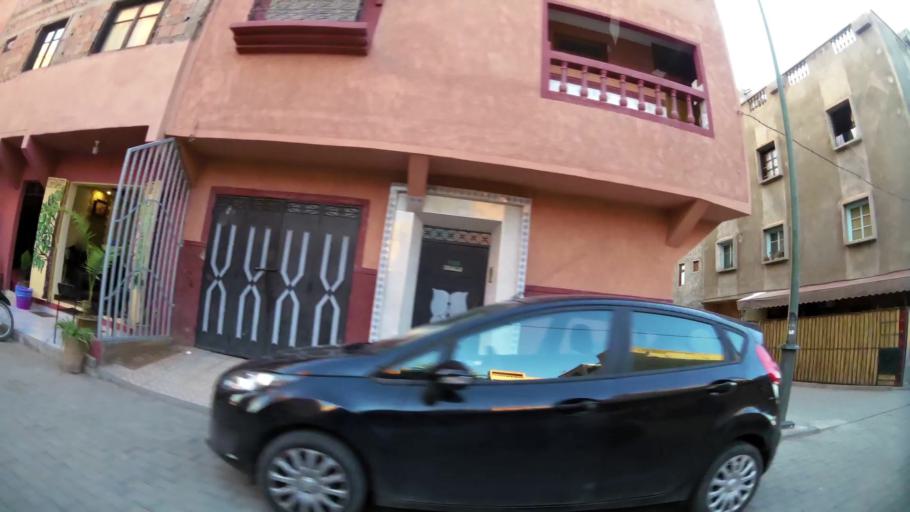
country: MA
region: Marrakech-Tensift-Al Haouz
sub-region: Marrakech
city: Marrakesh
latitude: 31.6400
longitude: -8.0365
